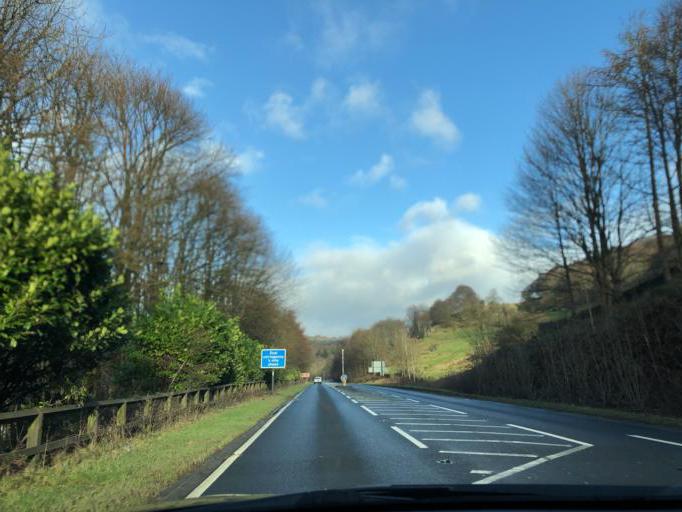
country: GB
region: England
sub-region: Cumbria
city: Grange-over-Sands
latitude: 54.2572
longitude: -2.9885
